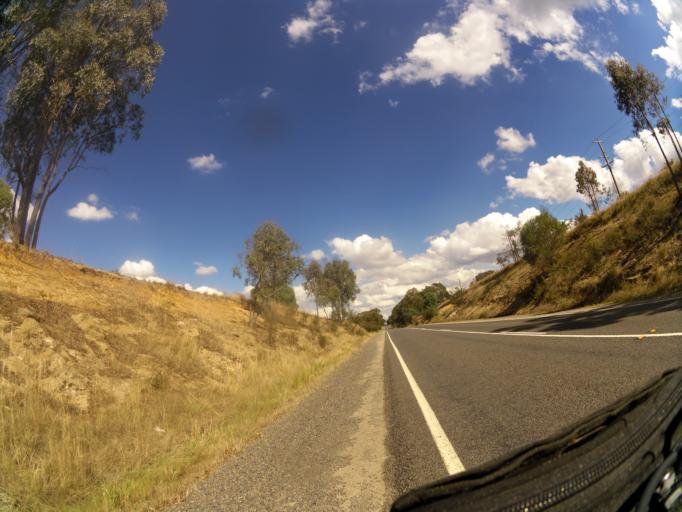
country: AU
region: Victoria
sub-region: Mansfield
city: Mansfield
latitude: -36.8809
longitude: 145.9942
